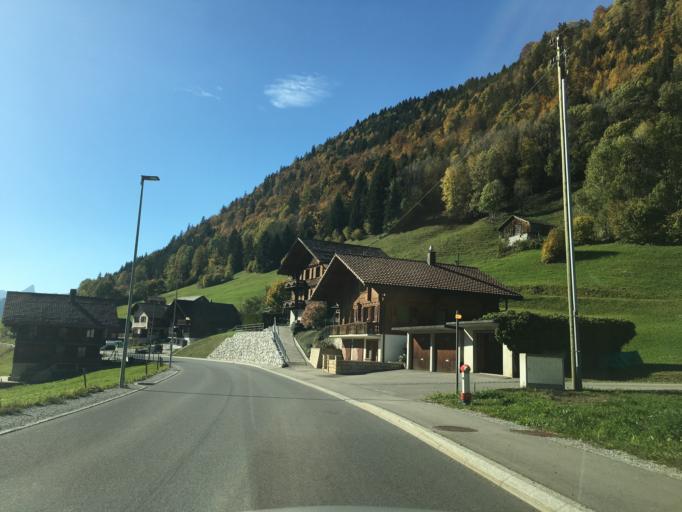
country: CH
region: Fribourg
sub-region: Gruyere District
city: Charmey
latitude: 46.6105
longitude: 7.2714
